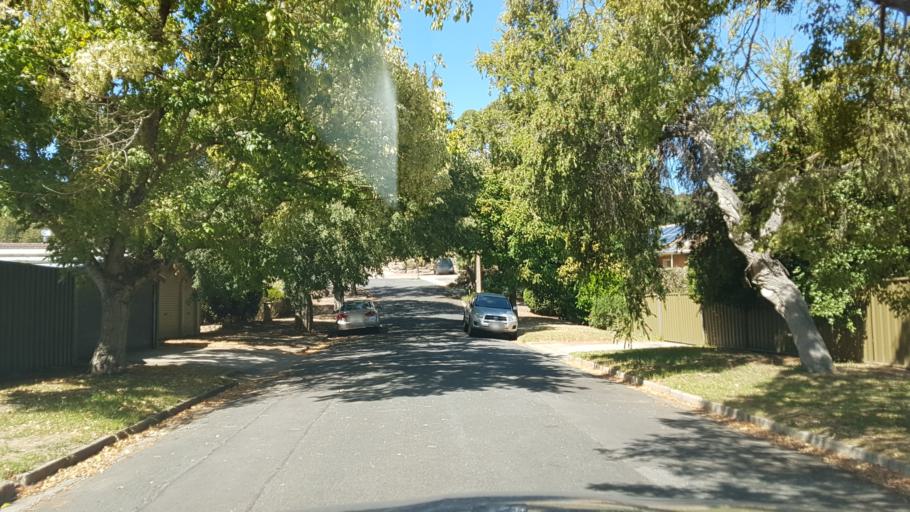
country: AU
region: South Australia
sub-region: Onkaparinga
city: Bedford Park
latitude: -35.0287
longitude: 138.5641
